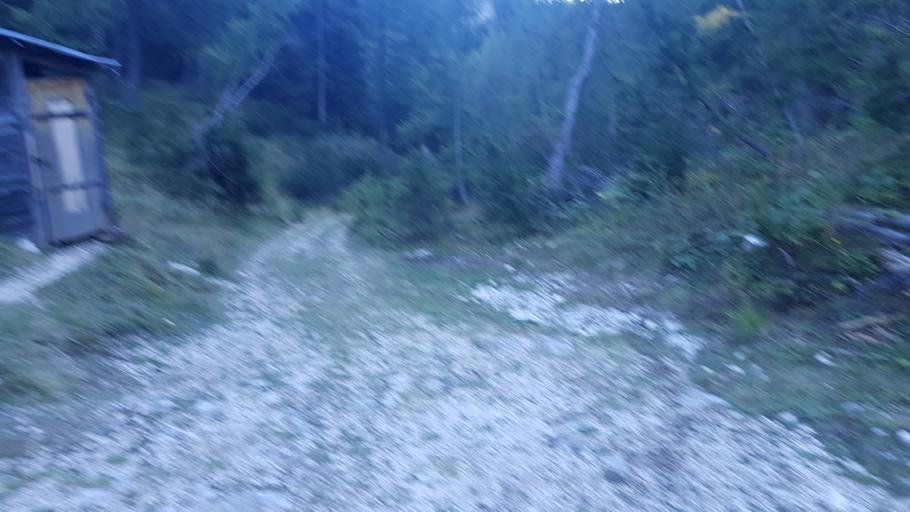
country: IT
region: Veneto
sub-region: Provincia di Belluno
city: Fusine
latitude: 46.3703
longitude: 12.0809
